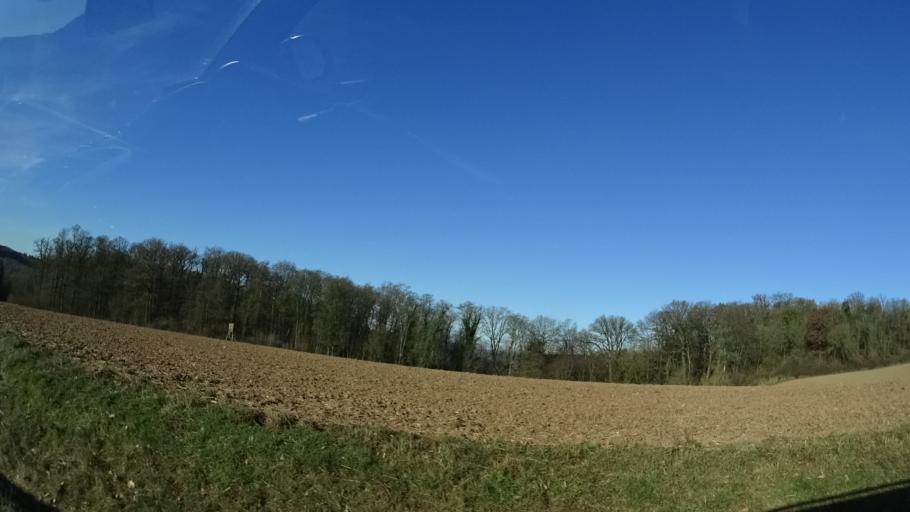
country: DE
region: Rheinland-Pfalz
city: Ruppertsecken
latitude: 49.6394
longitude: 7.8794
